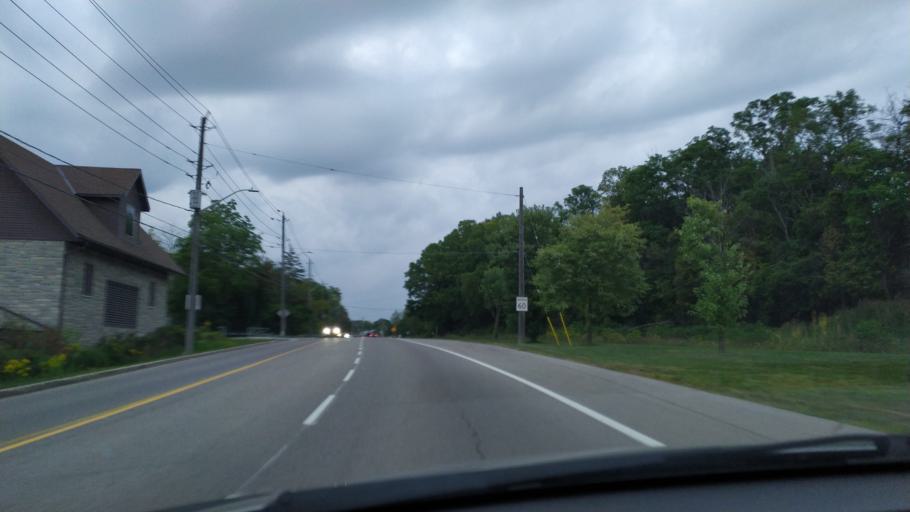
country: CA
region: Ontario
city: Kitchener
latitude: 43.4242
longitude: -80.4127
